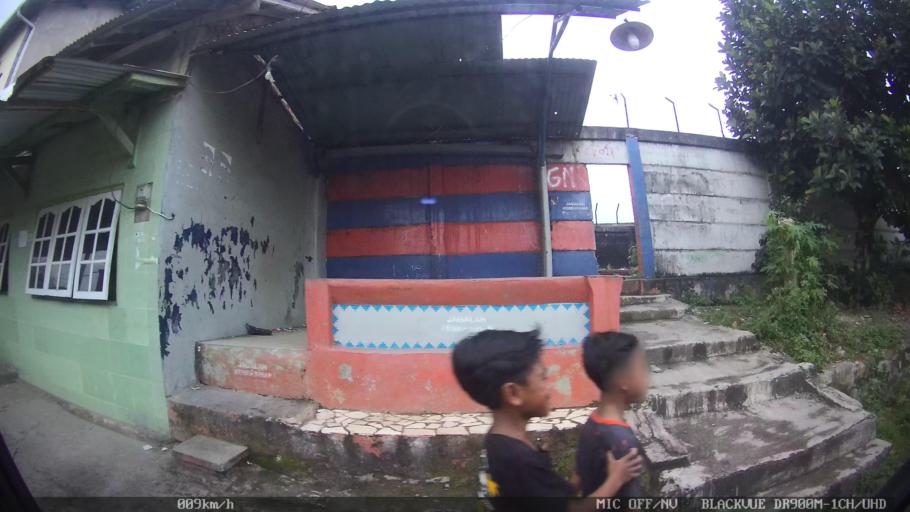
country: ID
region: Lampung
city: Bandarlampung
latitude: -5.4359
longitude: 105.2903
